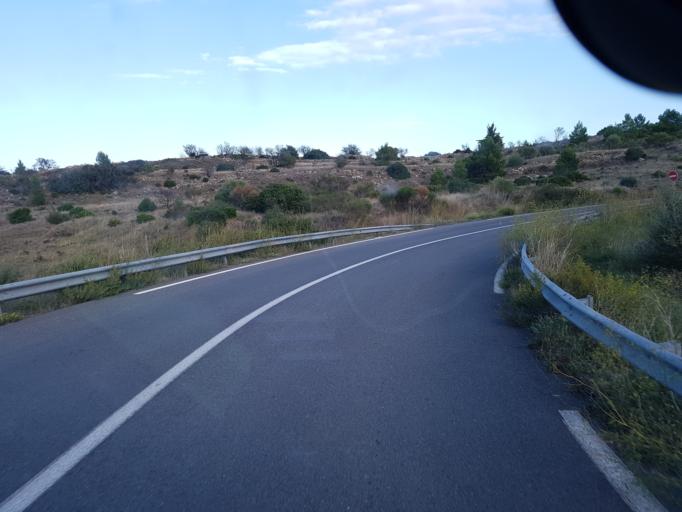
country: FR
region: Languedoc-Roussillon
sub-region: Departement de l'Aude
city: Leucate
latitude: 42.9310
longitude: 3.0153
